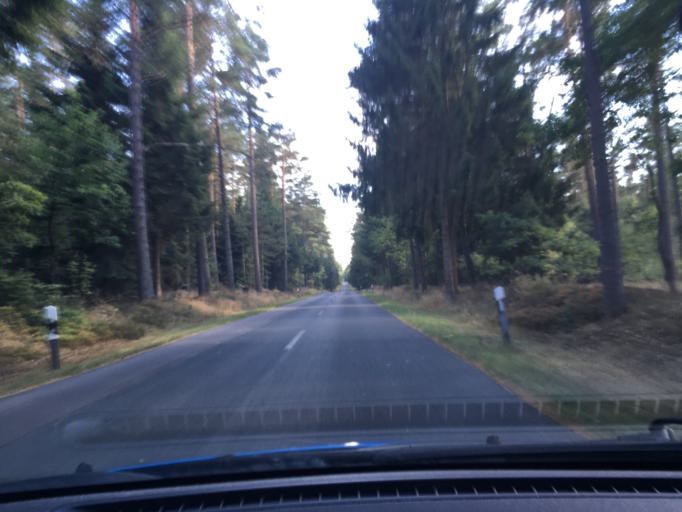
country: DE
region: Lower Saxony
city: Thomasburg
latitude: 53.2470
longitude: 10.7076
